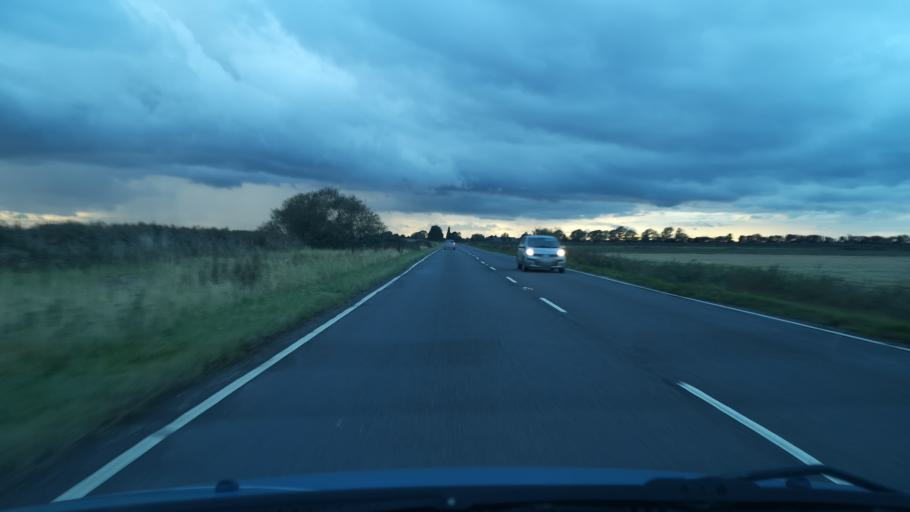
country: GB
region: England
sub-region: North Lincolnshire
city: Gunness
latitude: 53.5780
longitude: -0.7654
